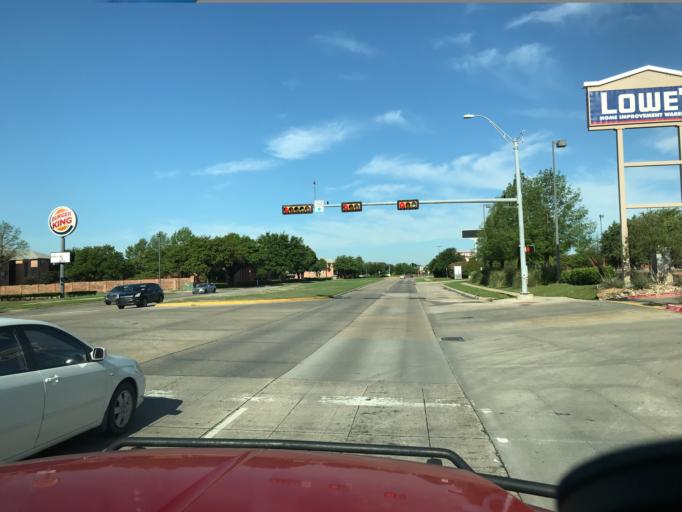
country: US
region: Texas
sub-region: Denton County
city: Lewisville
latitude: 33.0561
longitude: -97.0151
